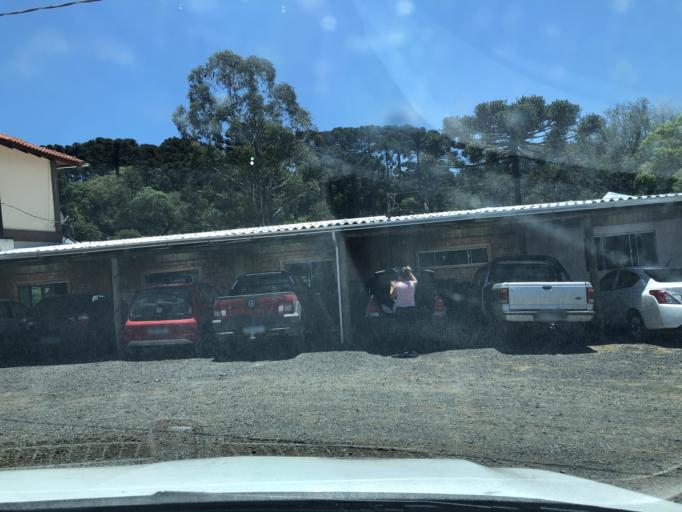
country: BR
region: Santa Catarina
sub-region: Lages
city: Lages
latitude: -27.7781
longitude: -50.3128
